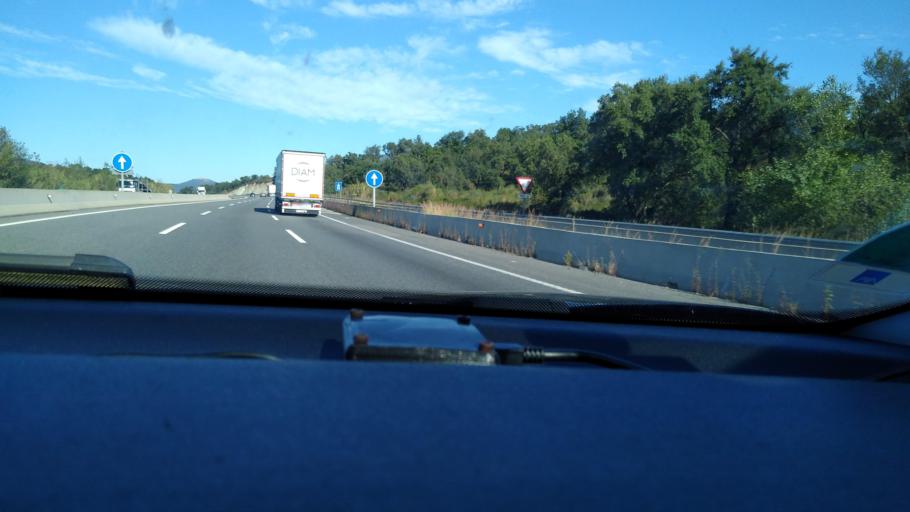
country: ES
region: Catalonia
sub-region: Provincia de Girona
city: Capmany
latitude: 42.3686
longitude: 2.8906
